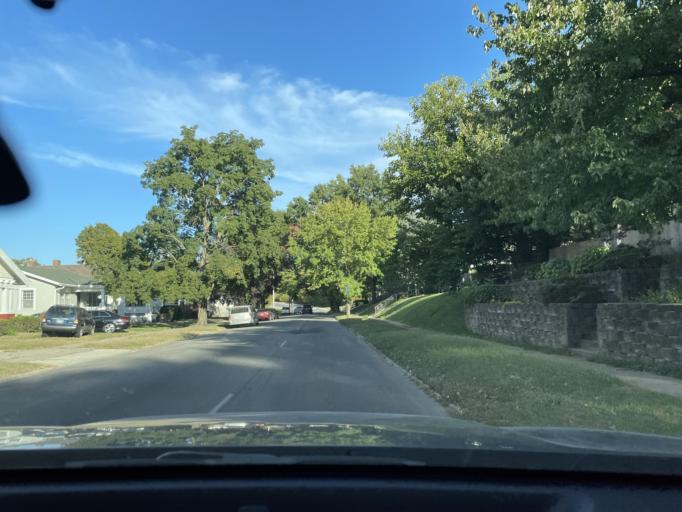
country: US
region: Missouri
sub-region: Buchanan County
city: Saint Joseph
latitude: 39.7683
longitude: -94.8174
